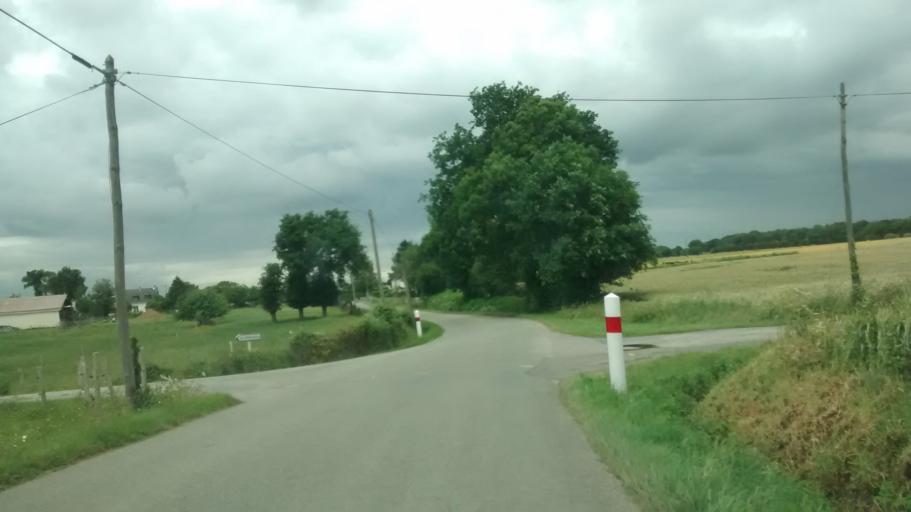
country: FR
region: Brittany
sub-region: Departement d'Ille-et-Vilaine
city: Sixt-sur-Aff
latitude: 47.7946
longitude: -2.1062
